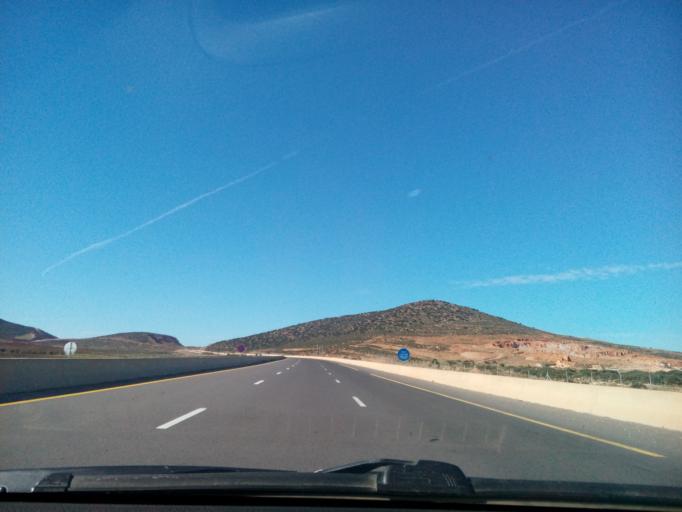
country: DZ
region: Tlemcen
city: Sidi Abdelli
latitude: 35.0202
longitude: -1.1172
